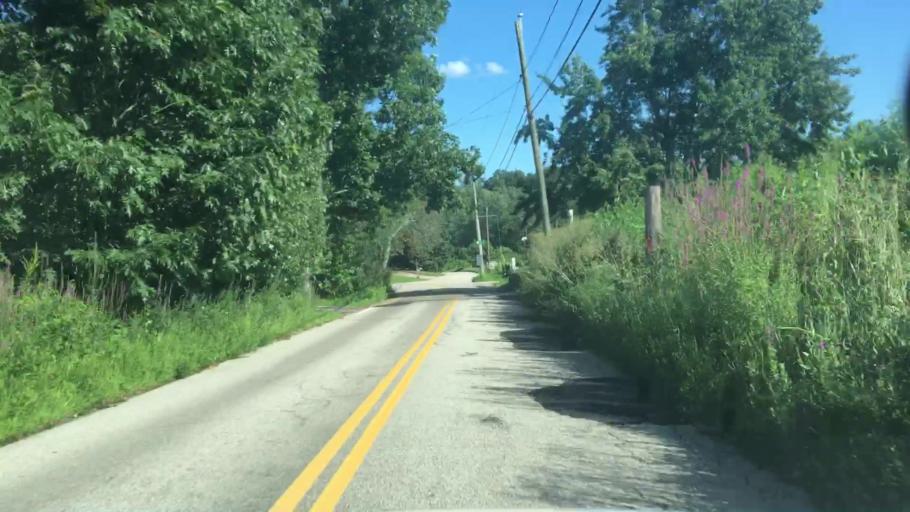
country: US
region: New Hampshire
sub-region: Strafford County
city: Dover
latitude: 43.1568
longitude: -70.8682
